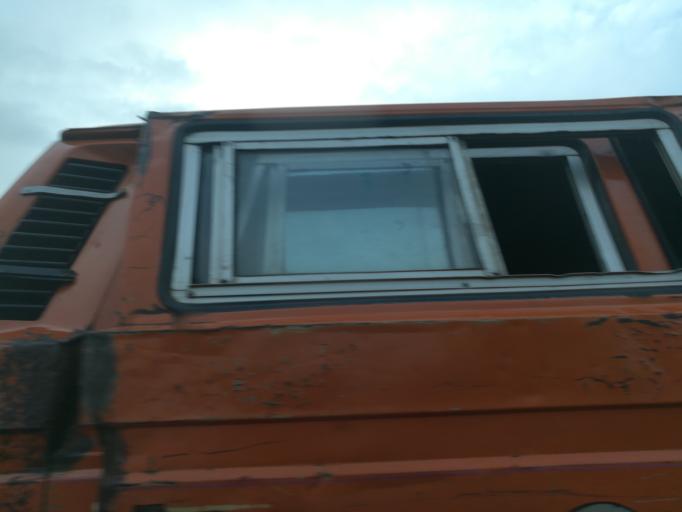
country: NG
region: Lagos
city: Ifako
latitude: 6.6369
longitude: 3.3685
